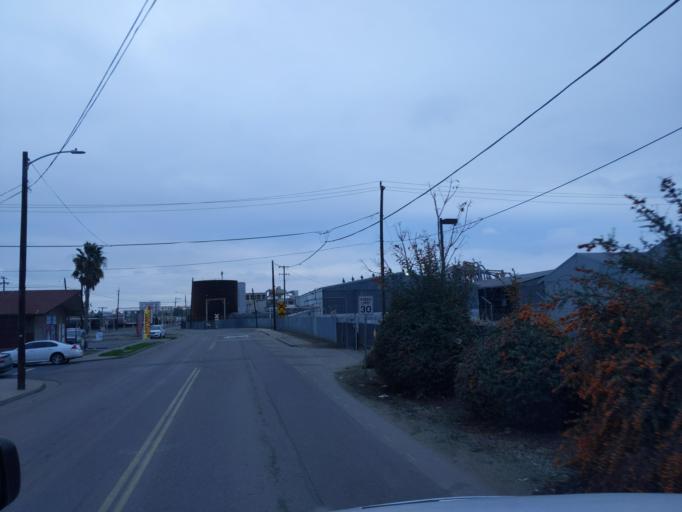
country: US
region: California
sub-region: San Joaquin County
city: Stockton
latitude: 37.9466
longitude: -121.3123
